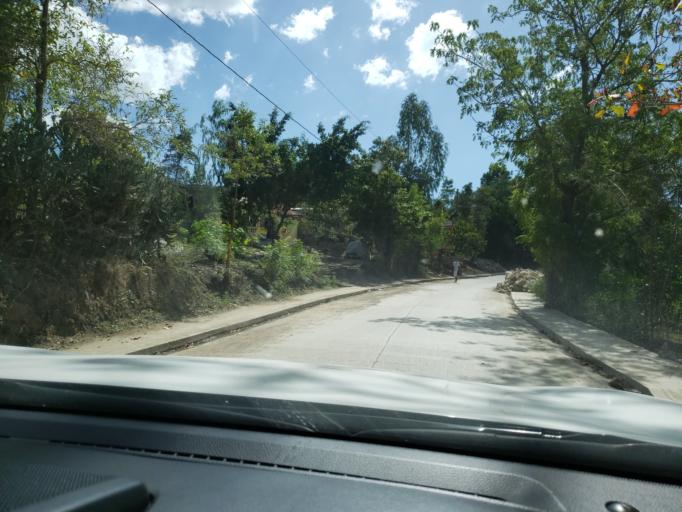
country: HT
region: Grandans
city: Anse-a-Veau
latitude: 18.4526
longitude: -73.3796
